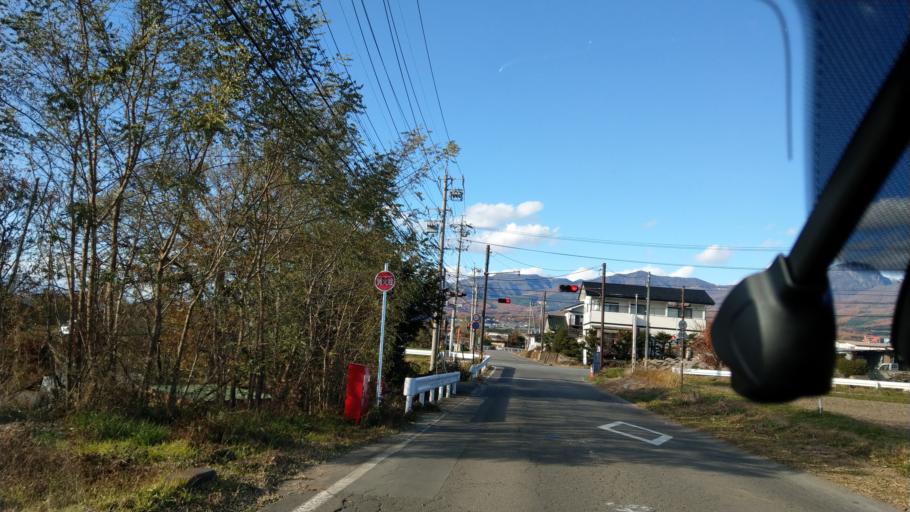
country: JP
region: Nagano
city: Komoro
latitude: 36.3045
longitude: 138.4692
